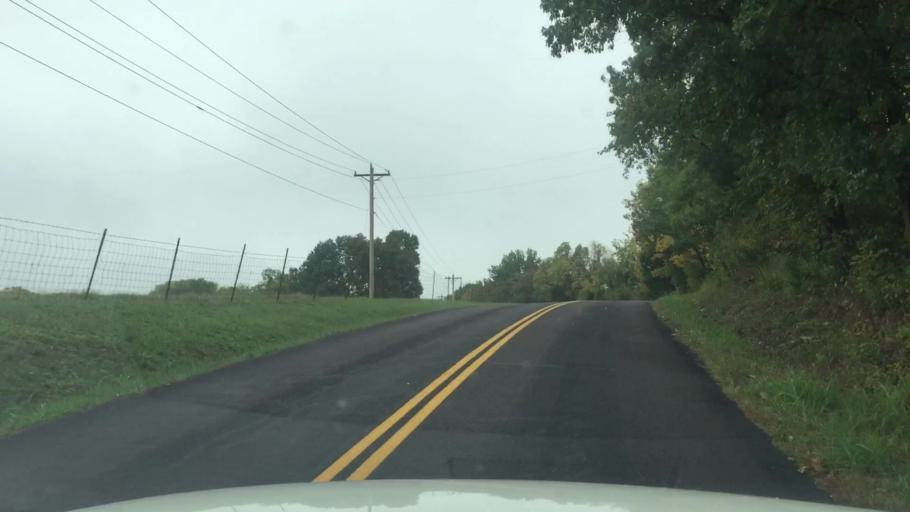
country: US
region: Missouri
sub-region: Boone County
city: Ashland
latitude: 38.8221
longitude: -92.3481
